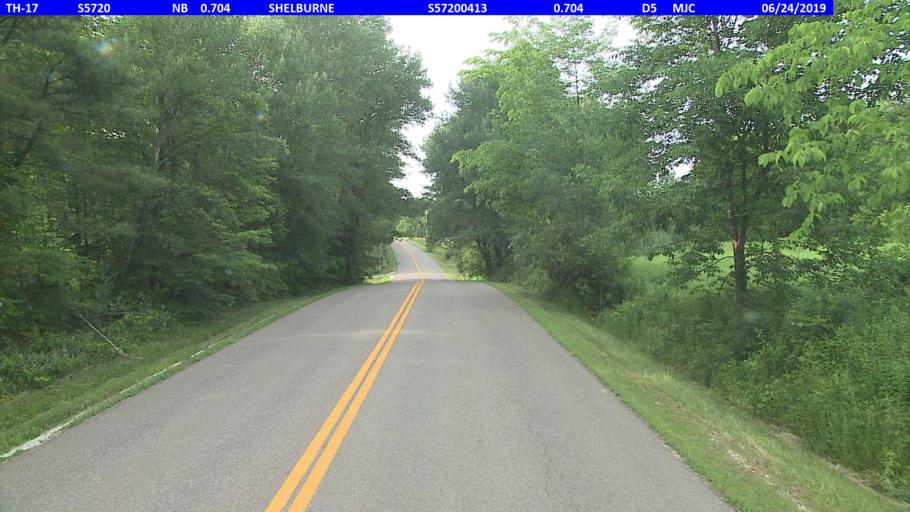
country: US
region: Vermont
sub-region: Chittenden County
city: Hinesburg
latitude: 44.3678
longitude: -73.2015
